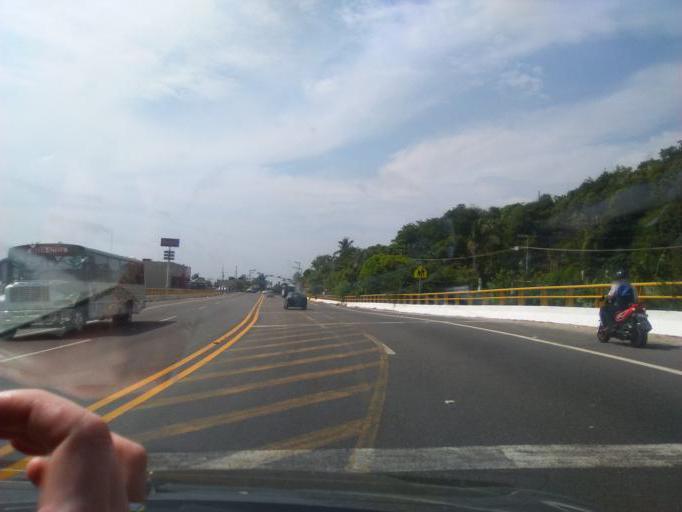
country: MX
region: Guerrero
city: Acapulco de Juarez
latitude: 16.8752
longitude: -99.9366
